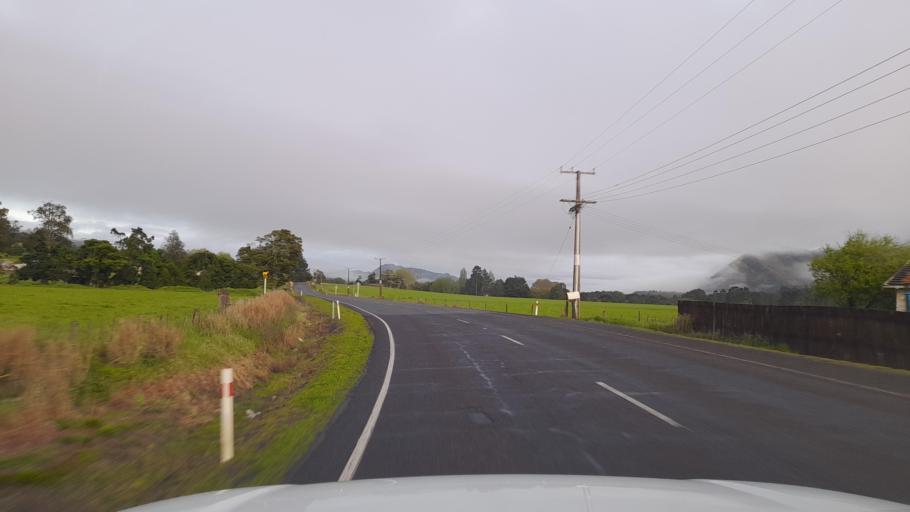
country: NZ
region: Northland
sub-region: Kaipara District
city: Dargaville
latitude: -35.7082
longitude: 173.9384
